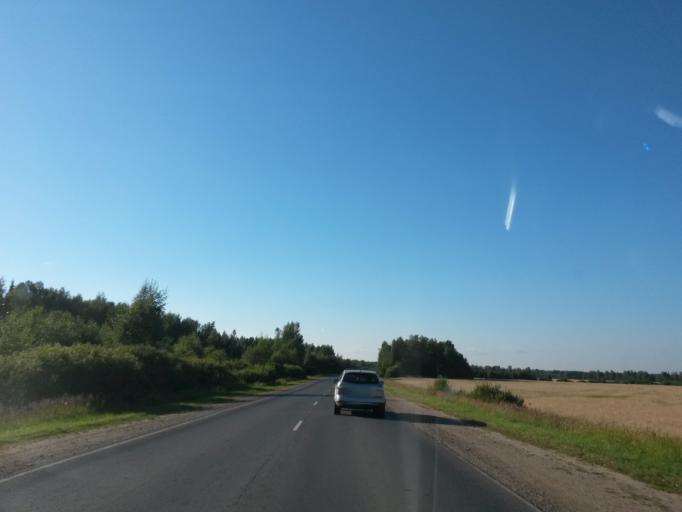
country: RU
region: Ivanovo
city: Novo-Talitsy
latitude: 57.0325
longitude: 40.7503
